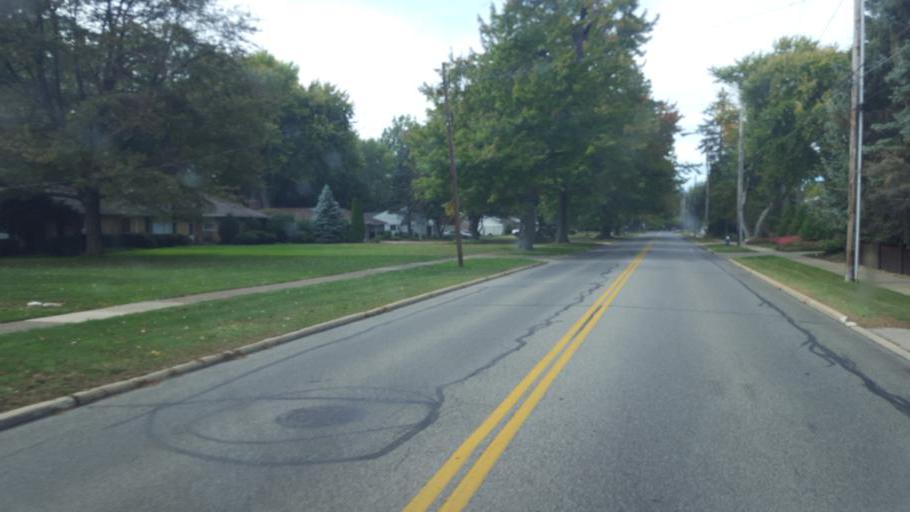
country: US
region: Ohio
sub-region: Cuyahoga County
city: Bay Village
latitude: 41.4956
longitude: -81.9553
